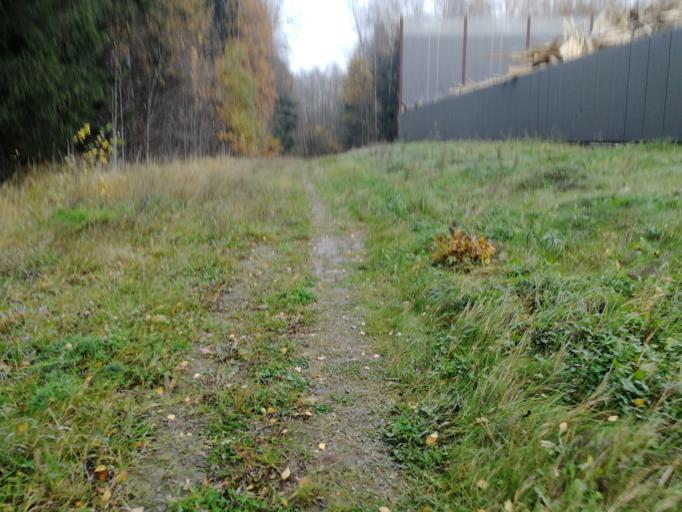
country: FI
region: Pirkanmaa
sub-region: Tampere
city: Tampere
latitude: 61.4481
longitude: 23.8903
